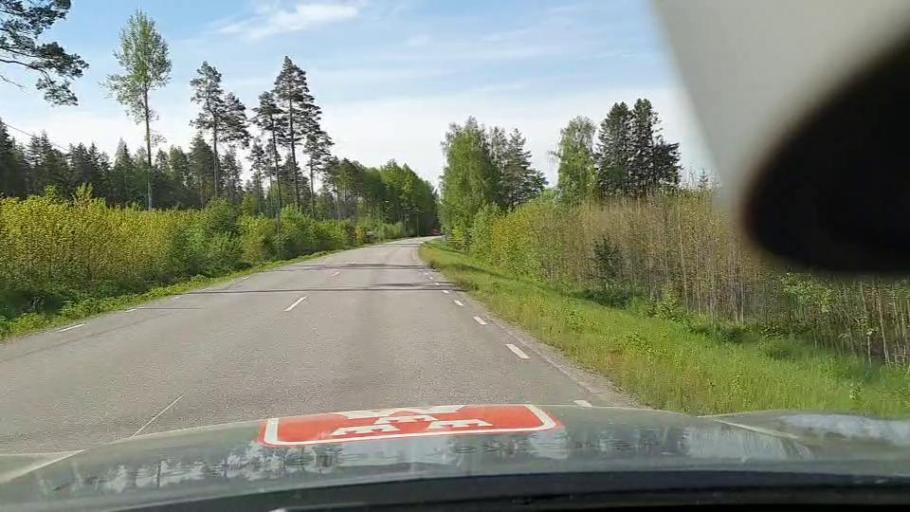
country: SE
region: Soedermanland
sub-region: Eskilstuna Kommun
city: Arla
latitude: 59.2956
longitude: 16.6770
